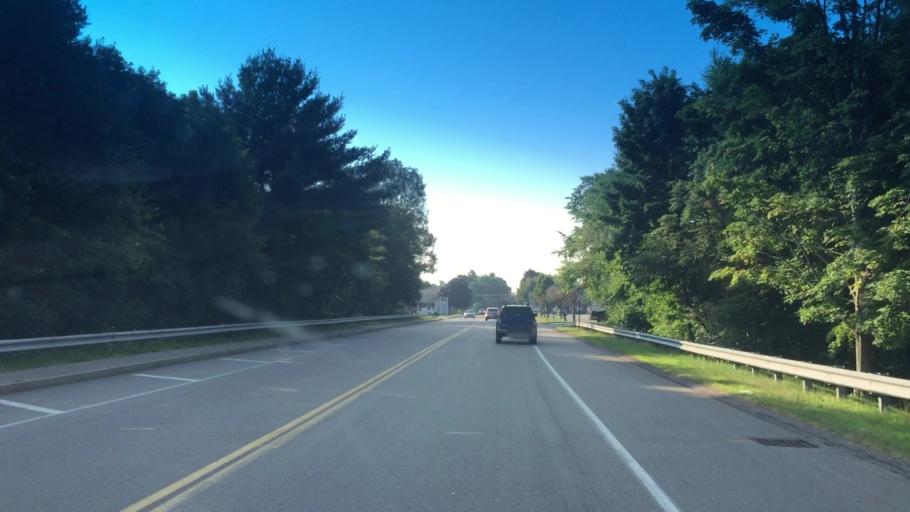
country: US
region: Massachusetts
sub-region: Norfolk County
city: Medfield
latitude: 42.1875
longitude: -71.3118
